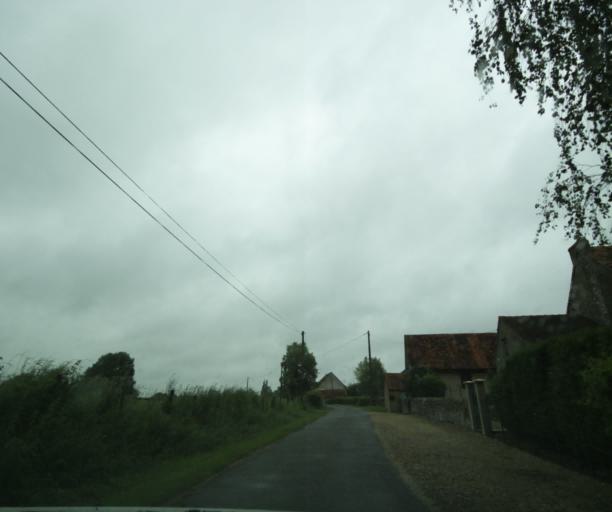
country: FR
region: Bourgogne
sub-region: Departement de Saone-et-Loire
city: Palinges
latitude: 46.5434
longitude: 4.1947
